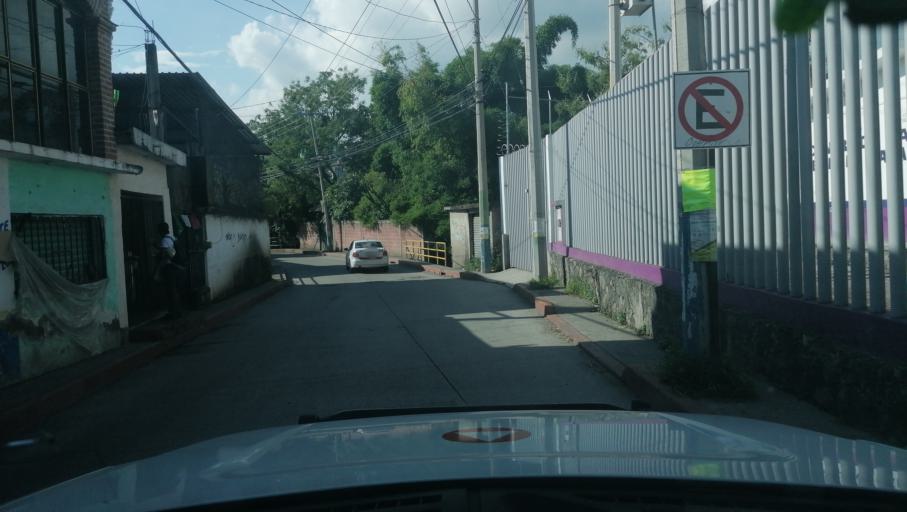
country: MX
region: Morelos
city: Emiliano Zapata
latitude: 18.8362
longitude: -99.1851
